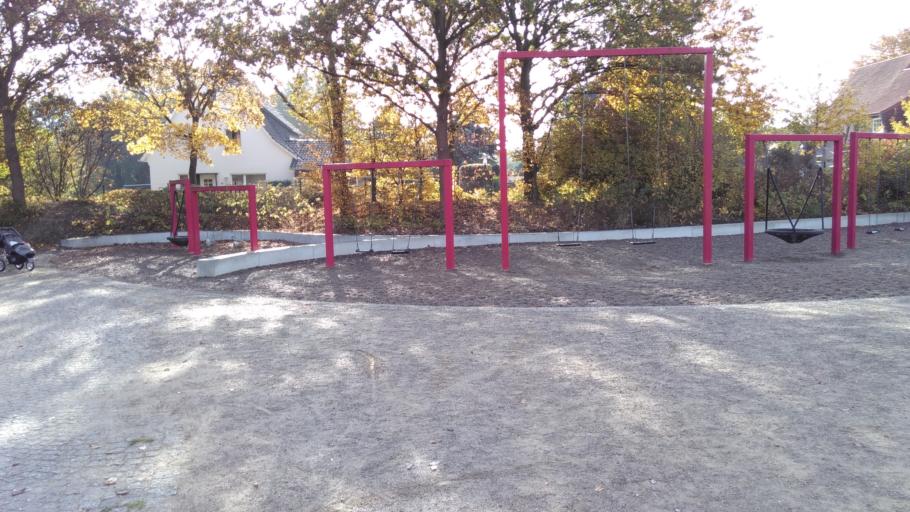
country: DE
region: North Rhine-Westphalia
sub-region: Regierungsbezirk Detmold
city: Rheda-Wiedenbruck
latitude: 51.8436
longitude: 8.2998
